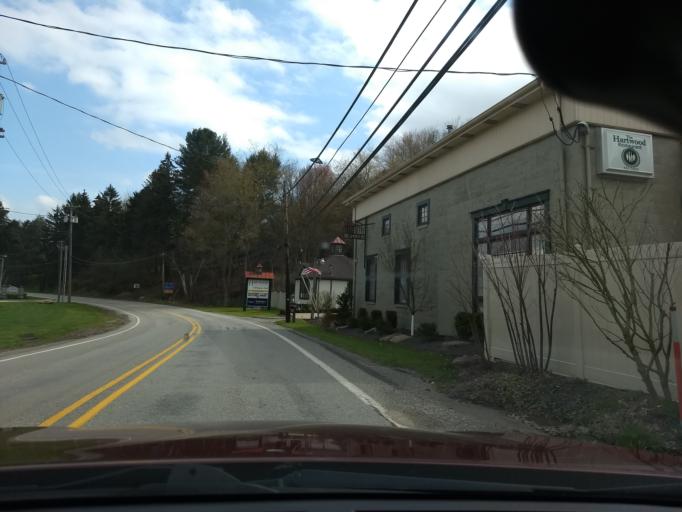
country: US
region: Pennsylvania
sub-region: Allegheny County
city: Allison Park
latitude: 40.5547
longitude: -79.9185
